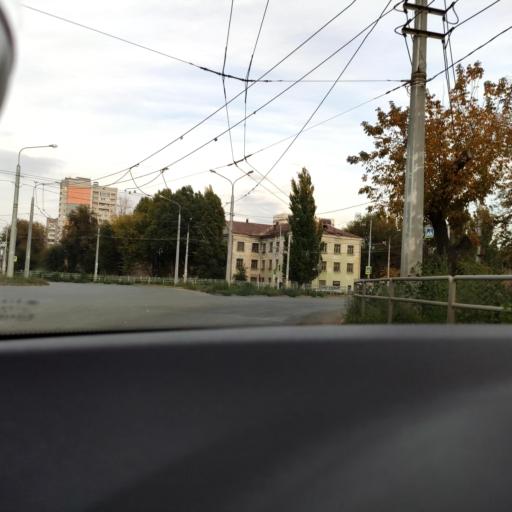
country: RU
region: Samara
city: Smyshlyayevka
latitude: 53.2060
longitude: 50.2765
